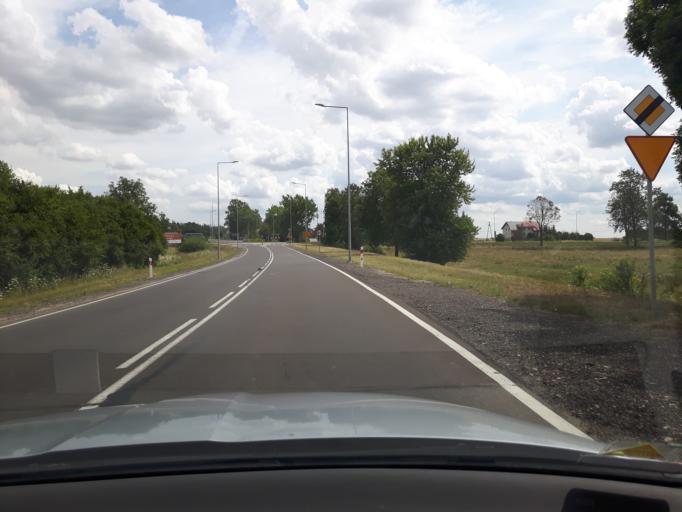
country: PL
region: Warmian-Masurian Voivodeship
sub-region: Powiat nidzicki
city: Nidzica
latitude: 53.3596
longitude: 20.4002
